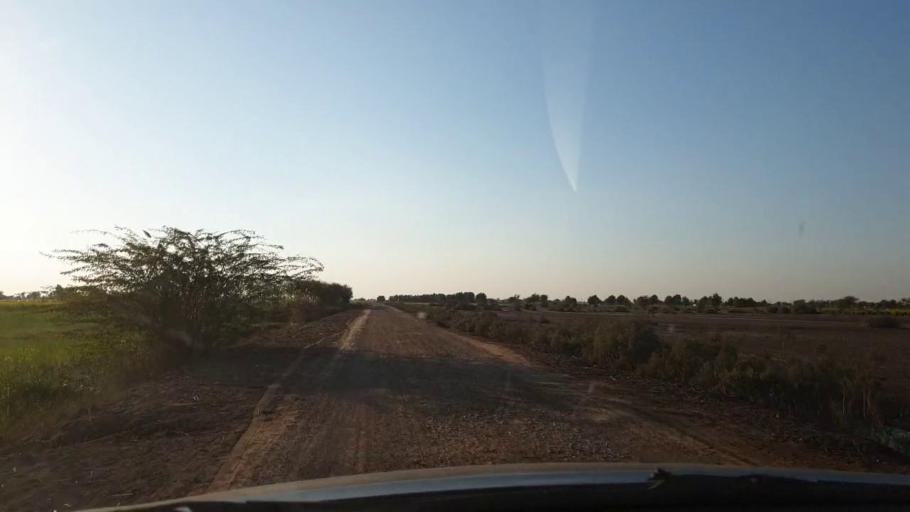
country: PK
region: Sindh
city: Tando Mittha Khan
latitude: 25.8323
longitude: 69.1688
